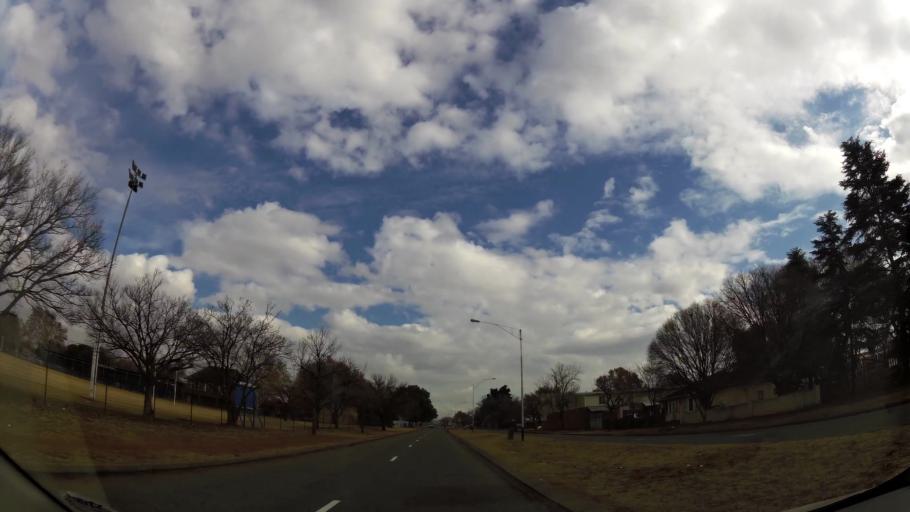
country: ZA
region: Gauteng
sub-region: Sedibeng District Municipality
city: Meyerton
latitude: -26.5596
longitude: 28.0134
